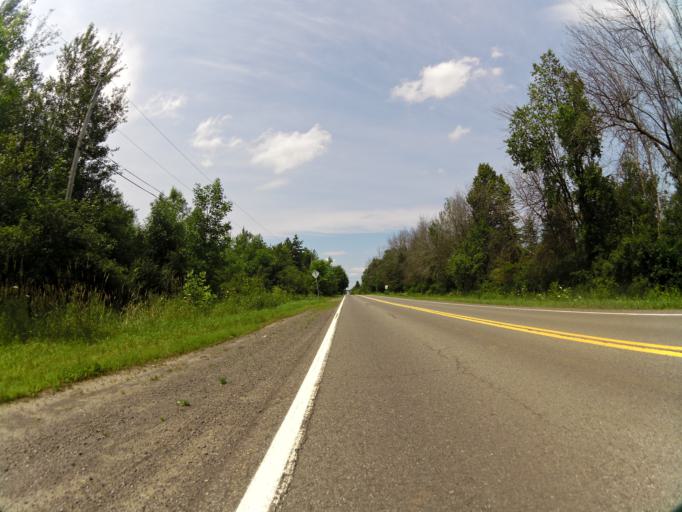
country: CA
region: Ontario
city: Ottawa
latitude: 45.2820
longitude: -75.6295
